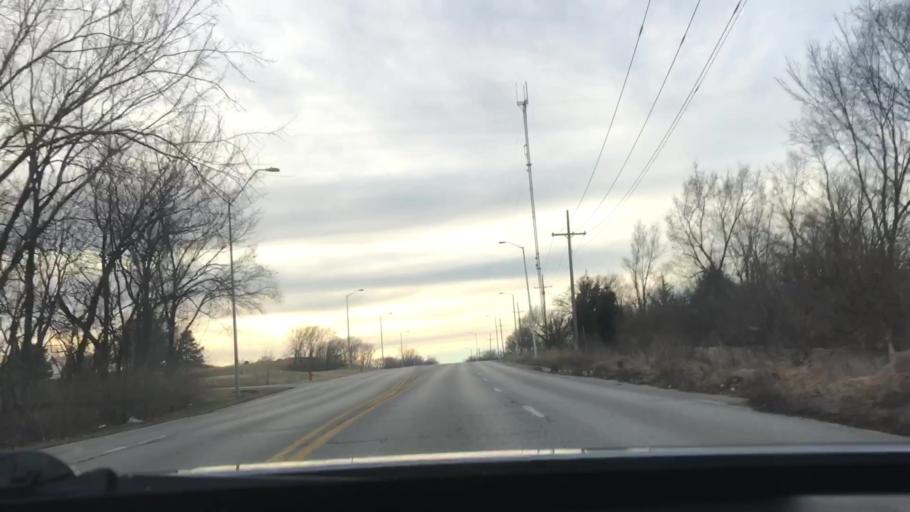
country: US
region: Missouri
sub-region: Jackson County
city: Sugar Creek
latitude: 39.0829
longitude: -94.5046
